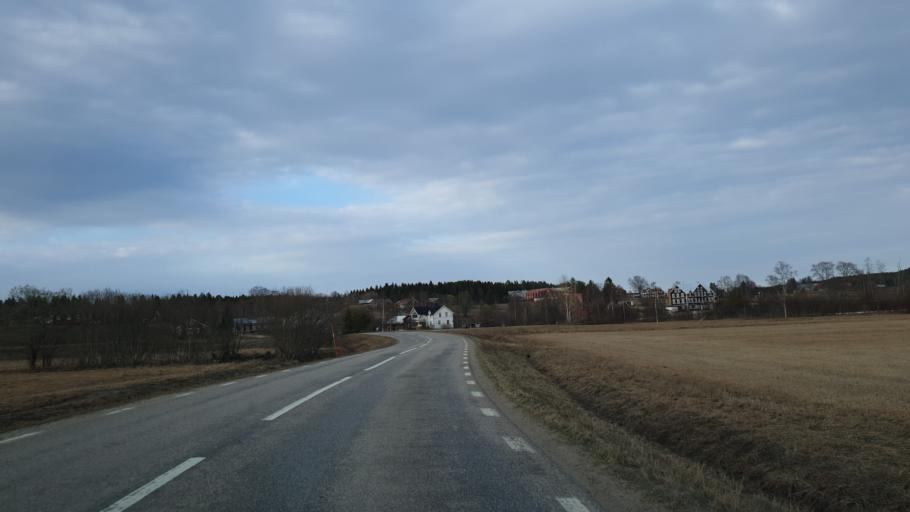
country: SE
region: Gaevleborg
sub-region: Nordanstigs Kommun
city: Bergsjoe
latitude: 61.9772
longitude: 17.2620
